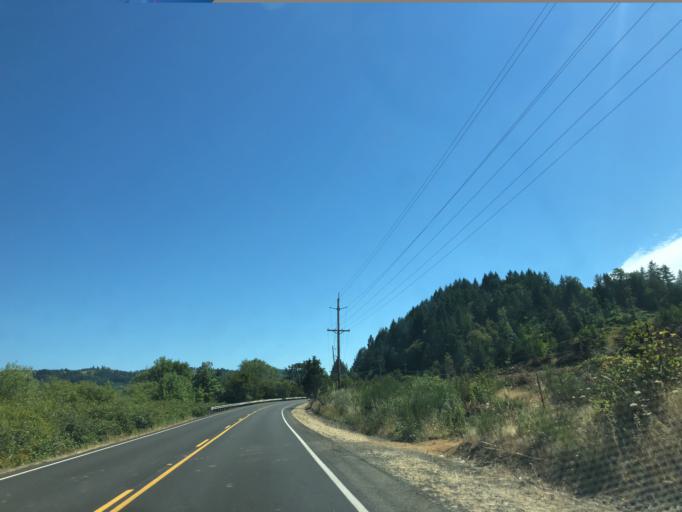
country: US
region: Oregon
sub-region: Douglas County
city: Yoncalla
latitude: 43.5836
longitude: -123.2805
